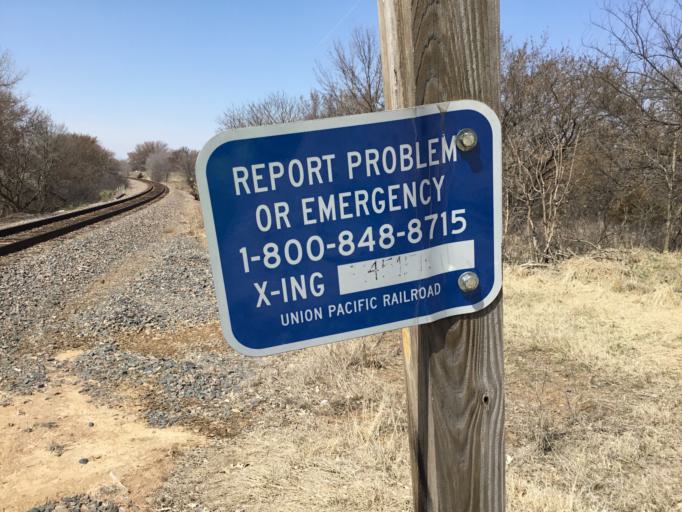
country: US
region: Kansas
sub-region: Ellsworth County
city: Ellsworth
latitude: 38.7356
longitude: -98.2458
